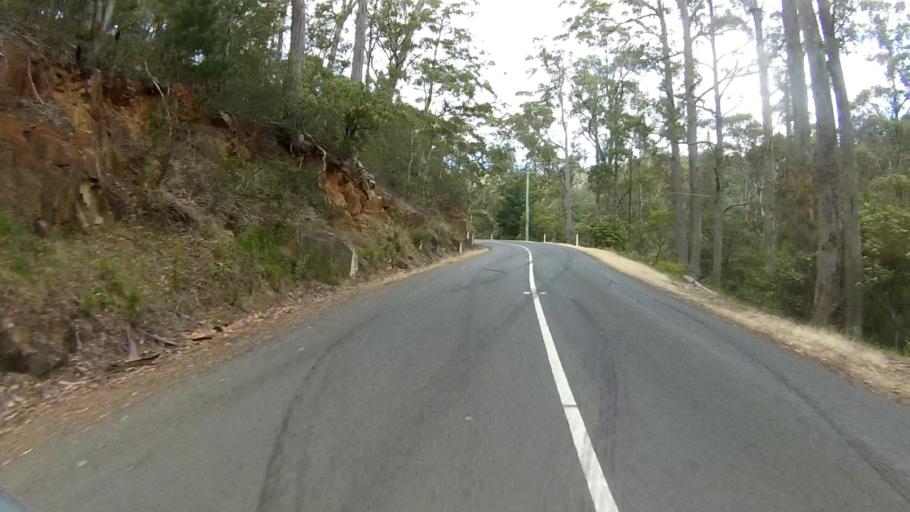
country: AU
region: Tasmania
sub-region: Kingborough
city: Margate
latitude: -42.9730
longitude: 147.1752
